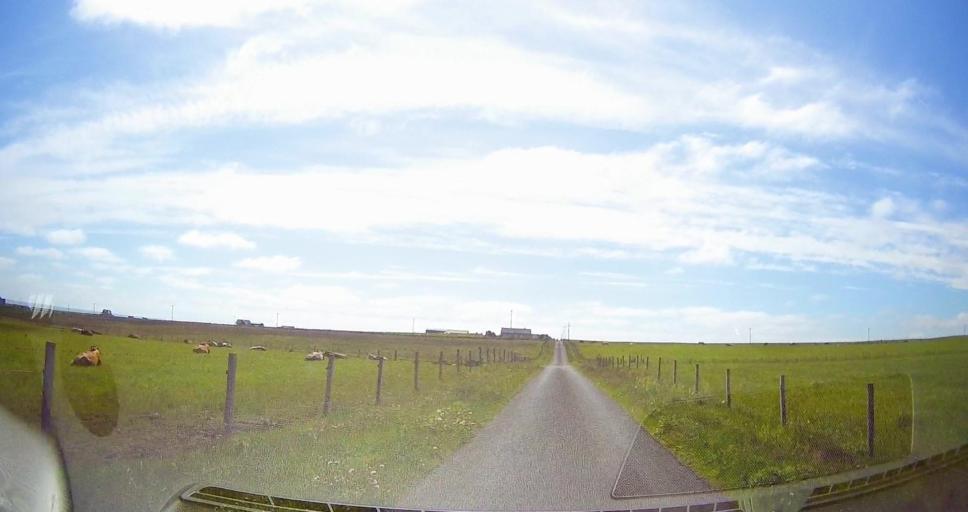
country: GB
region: Scotland
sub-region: Orkney Islands
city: Kirkwall
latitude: 58.8343
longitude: -2.9005
